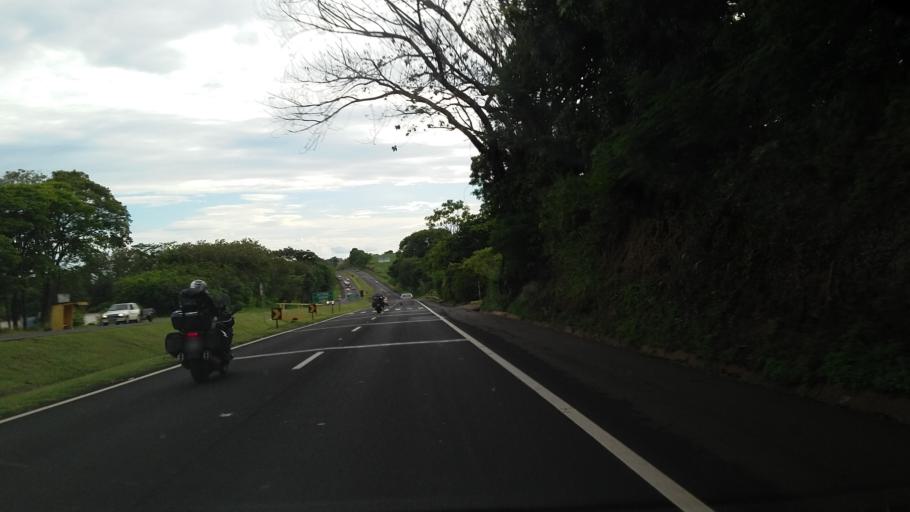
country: BR
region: Parana
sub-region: Paicandu
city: Paicandu
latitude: -23.5096
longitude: -52.0235
